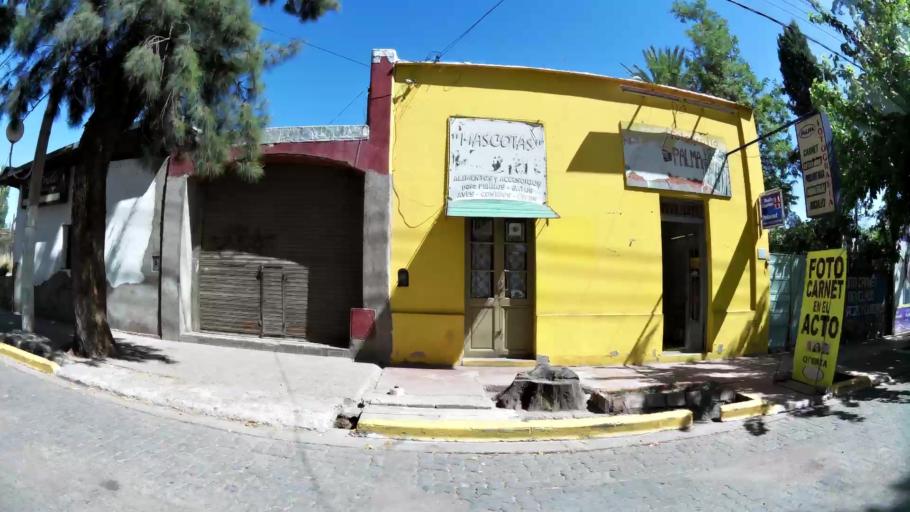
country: AR
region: Mendoza
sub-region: Departamento de Godoy Cruz
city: Godoy Cruz
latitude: -32.9651
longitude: -68.8540
